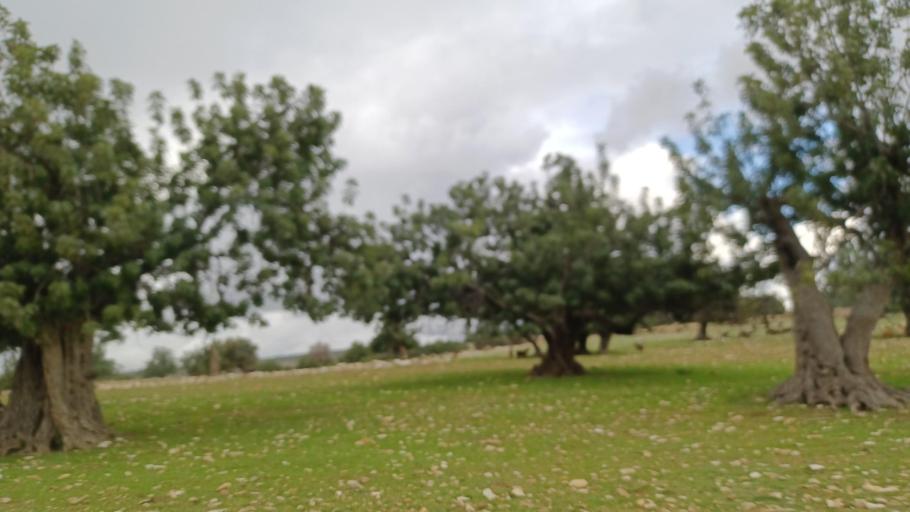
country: CY
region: Limassol
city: Sotira
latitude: 34.7240
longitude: 32.8273
